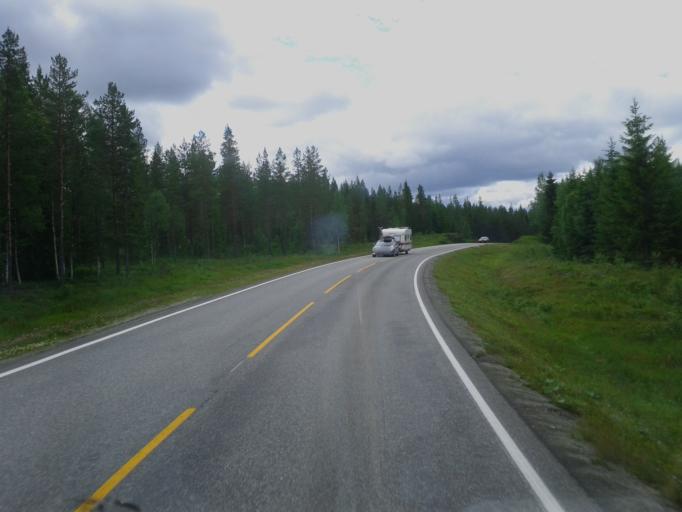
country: NO
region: Nord-Trondelag
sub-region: Hoylandet
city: Hoylandet
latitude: 64.6550
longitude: 12.6497
